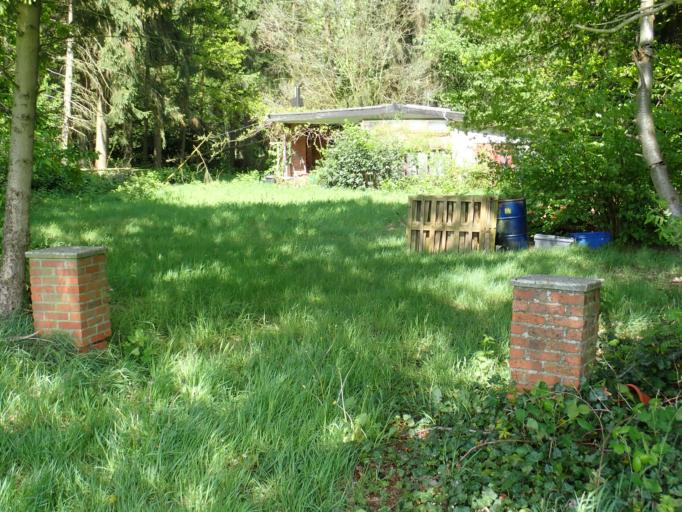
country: BE
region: Flanders
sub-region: Provincie Antwerpen
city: Lille
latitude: 51.2211
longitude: 4.8199
